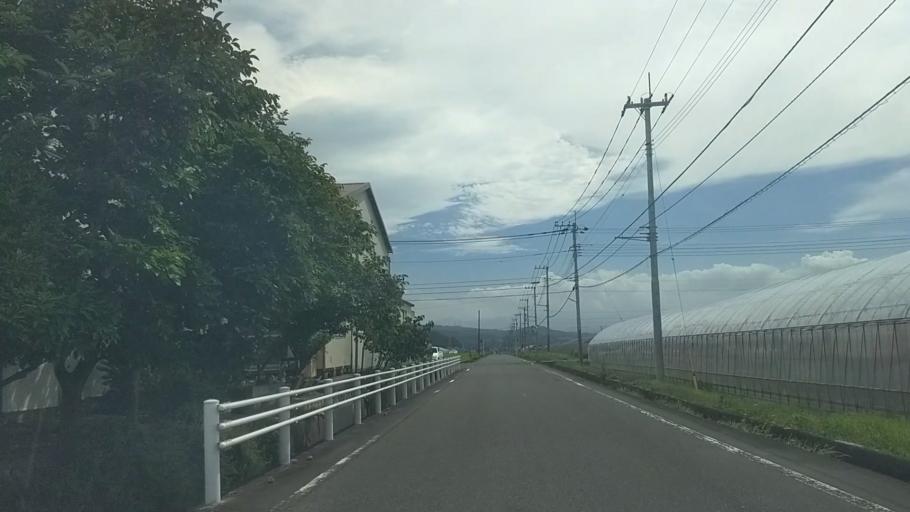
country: JP
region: Shizuoka
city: Mishima
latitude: 35.0698
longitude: 138.9444
